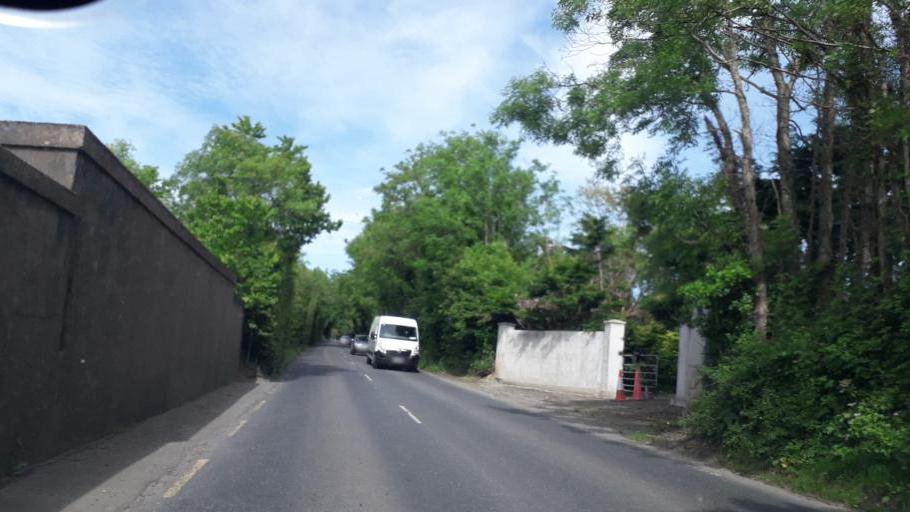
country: IE
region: Leinster
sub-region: Loch Garman
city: New Ross
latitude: 52.2773
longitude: -6.7254
